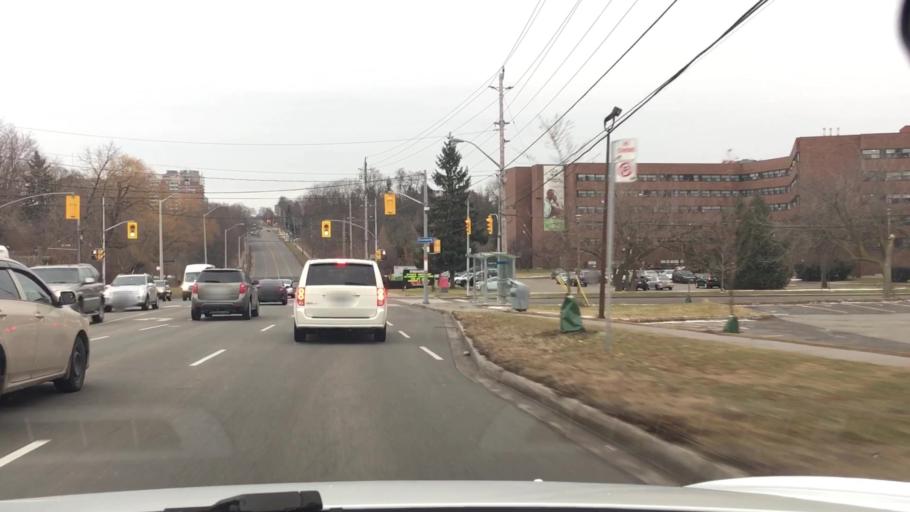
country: CA
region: Ontario
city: Scarborough
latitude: 43.7561
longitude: -79.2243
